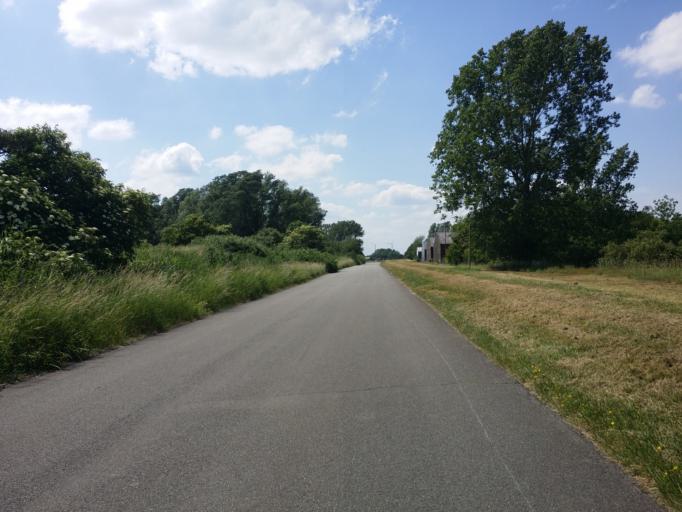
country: DE
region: Lower Saxony
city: Lemwerder
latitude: 53.1214
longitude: 8.6652
